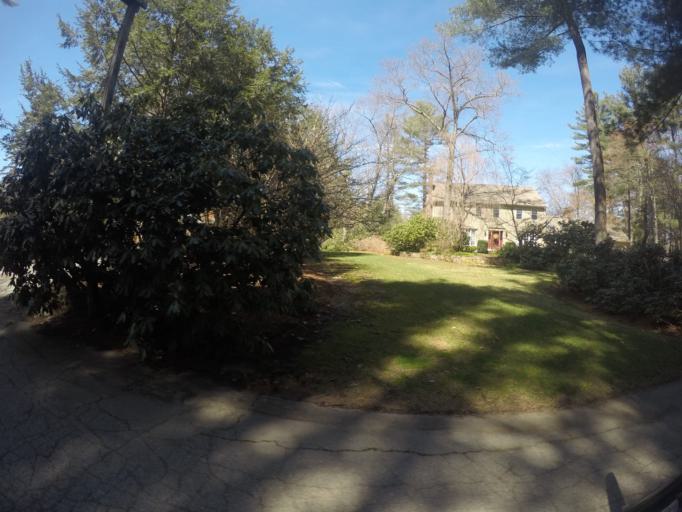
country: US
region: Massachusetts
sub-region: Bristol County
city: Easton
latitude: 42.0481
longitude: -71.0918
